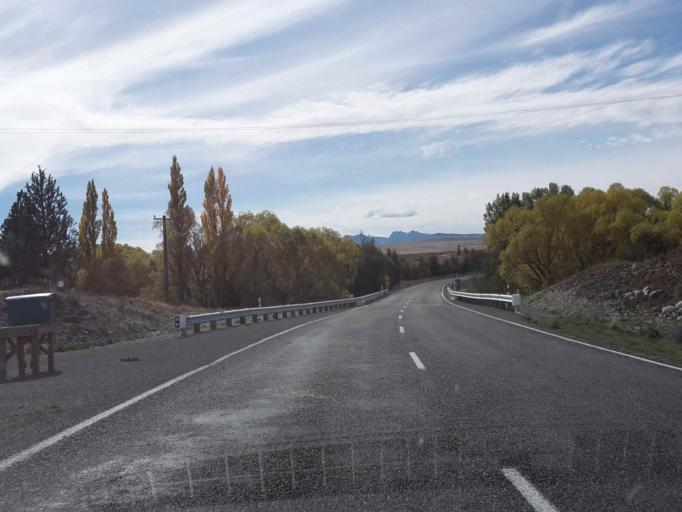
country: NZ
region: Canterbury
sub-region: Timaru District
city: Pleasant Point
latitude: -44.0882
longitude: 170.3489
